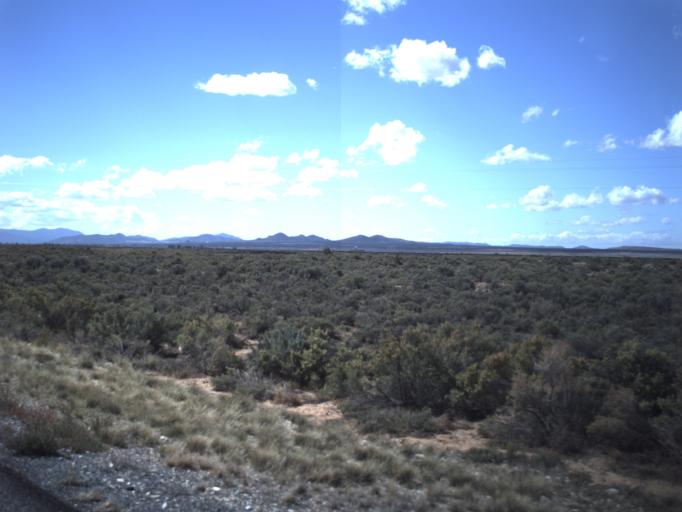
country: US
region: Utah
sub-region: Iron County
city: Enoch
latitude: 37.8362
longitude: -113.0497
